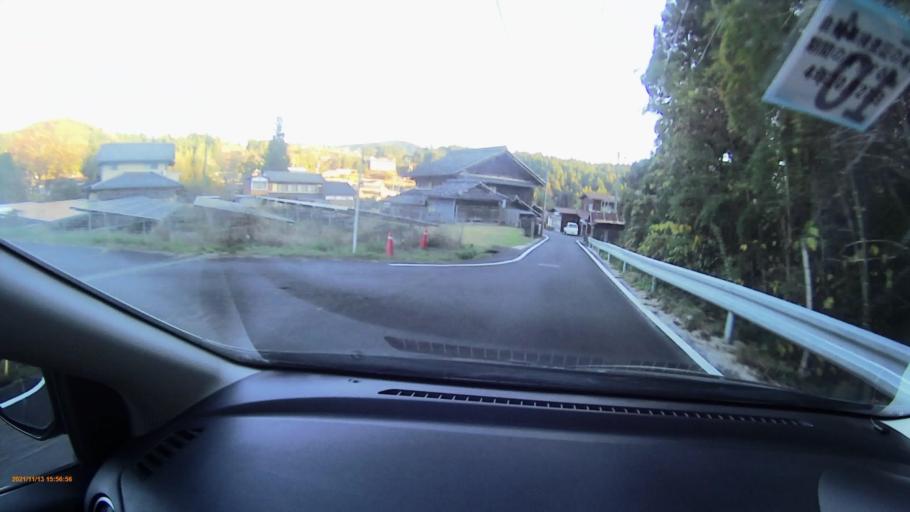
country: JP
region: Gifu
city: Nakatsugawa
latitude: 35.5915
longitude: 137.4575
